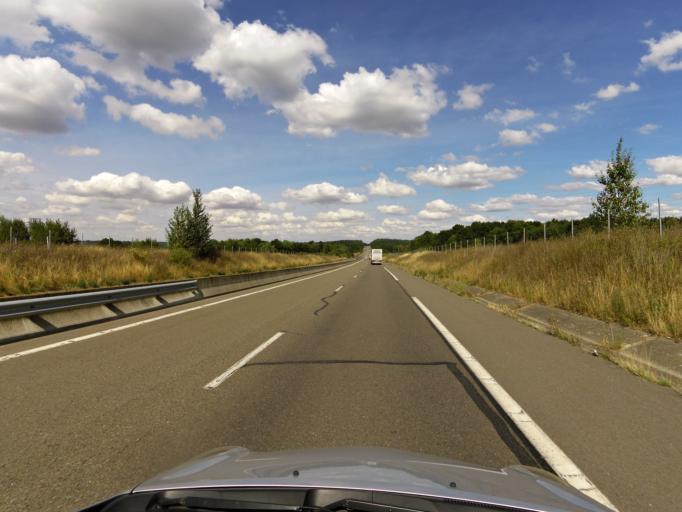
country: FR
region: Picardie
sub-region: Departement de l'Aisne
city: Vailly-sur-Aisne
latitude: 49.4775
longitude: 3.5341
